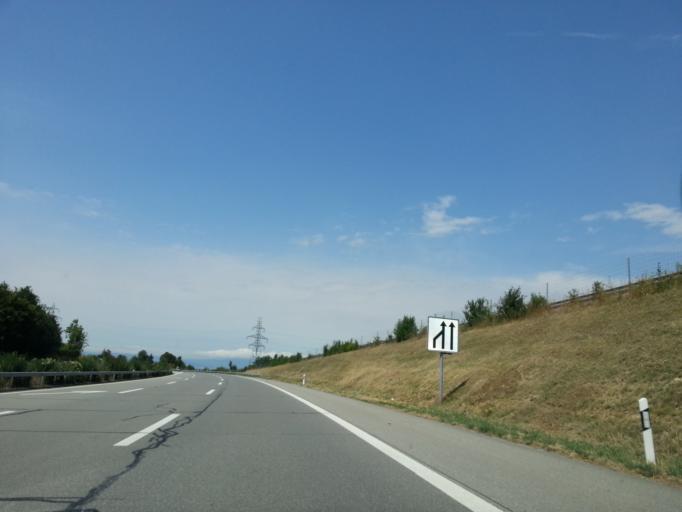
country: CH
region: Bern
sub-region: Bern-Mittelland District
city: Frauenkappelen
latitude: 46.9547
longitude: 7.3231
